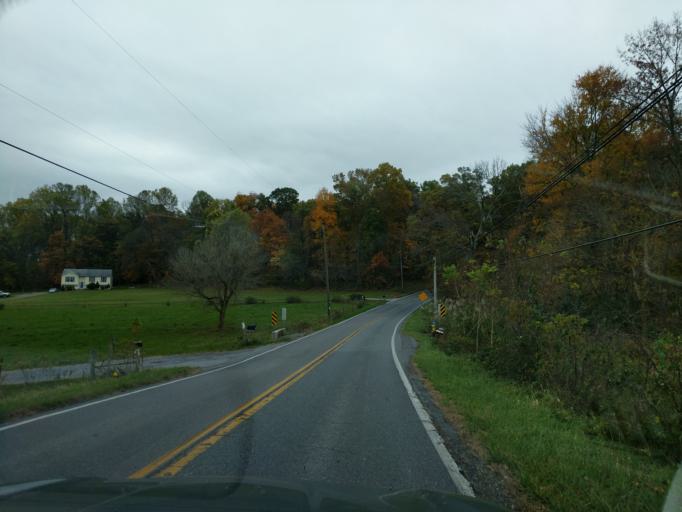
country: US
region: Maryland
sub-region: Frederick County
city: Spring Ridge
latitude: 39.4039
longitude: -77.2887
